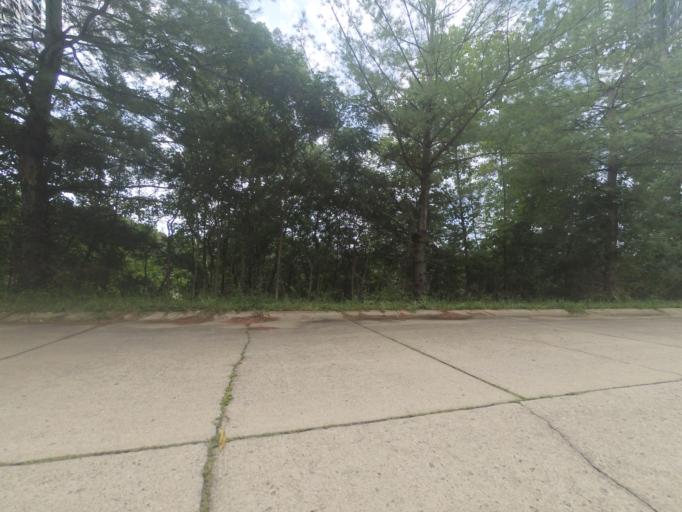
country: US
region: West Virginia
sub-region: Cabell County
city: Huntington
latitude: 38.3985
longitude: -82.4118
